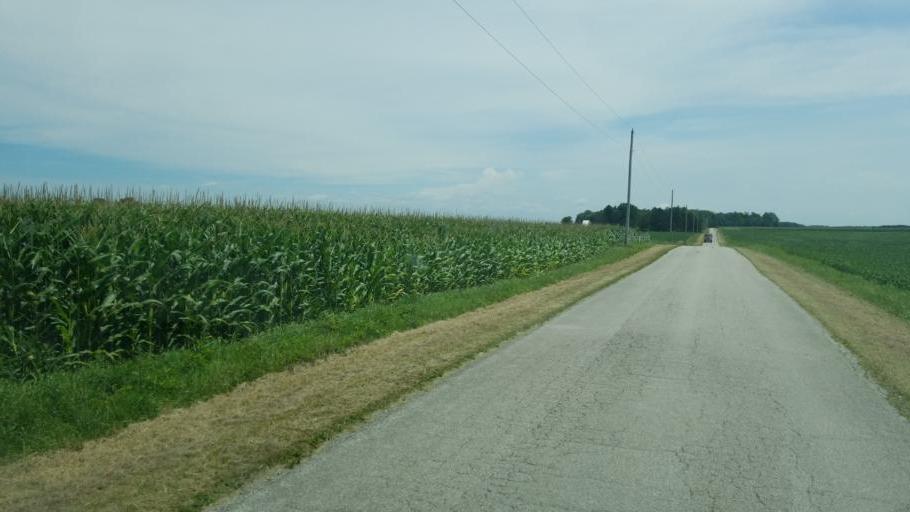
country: US
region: Ohio
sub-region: Crawford County
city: Bucyrus
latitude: 40.8782
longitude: -82.9124
